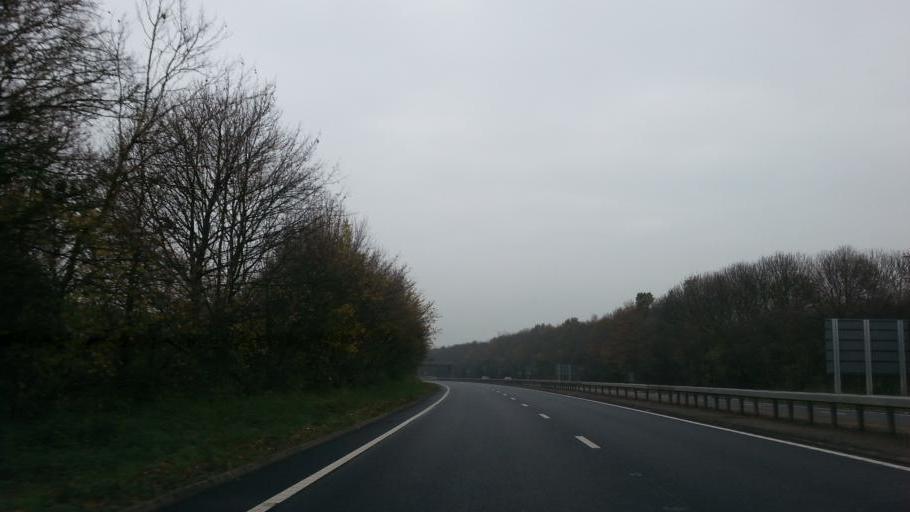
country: GB
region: England
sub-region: Cambridgeshire
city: Yaxley
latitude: 52.5389
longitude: -0.3033
